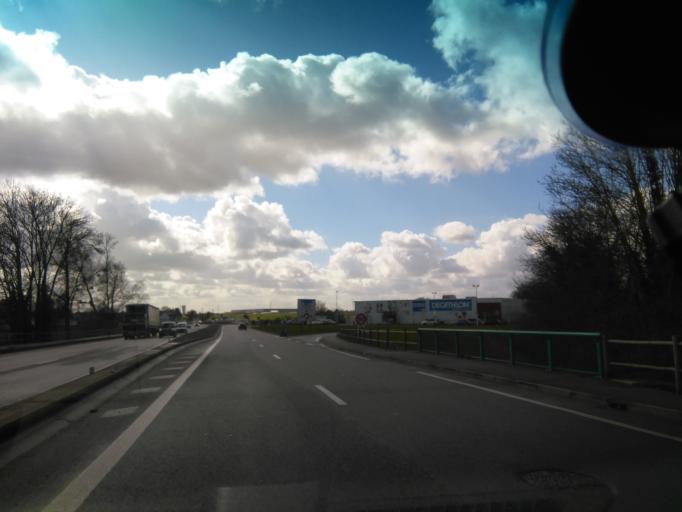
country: FR
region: Lower Normandy
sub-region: Departement de l'Orne
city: Argentan
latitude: 48.7312
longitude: -0.0372
